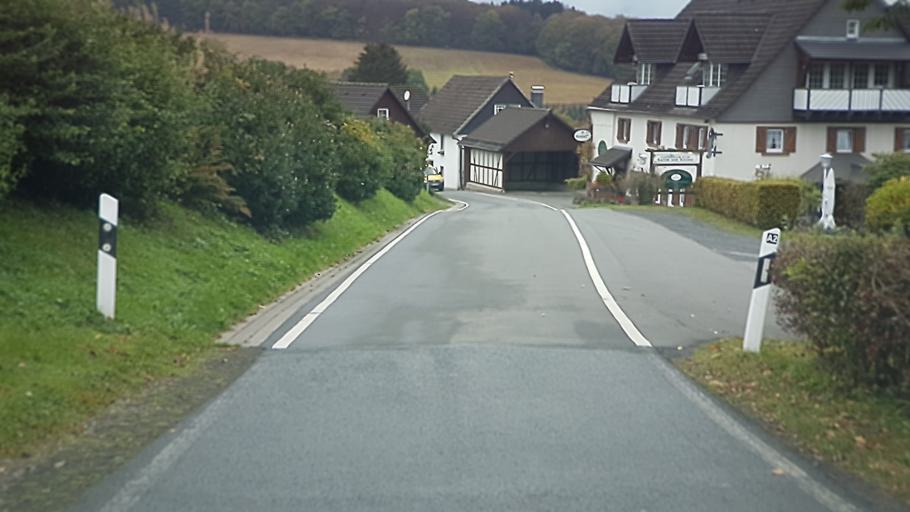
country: DE
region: North Rhine-Westphalia
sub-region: Regierungsbezirk Arnsberg
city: Herscheid
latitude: 51.1613
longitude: 7.6995
